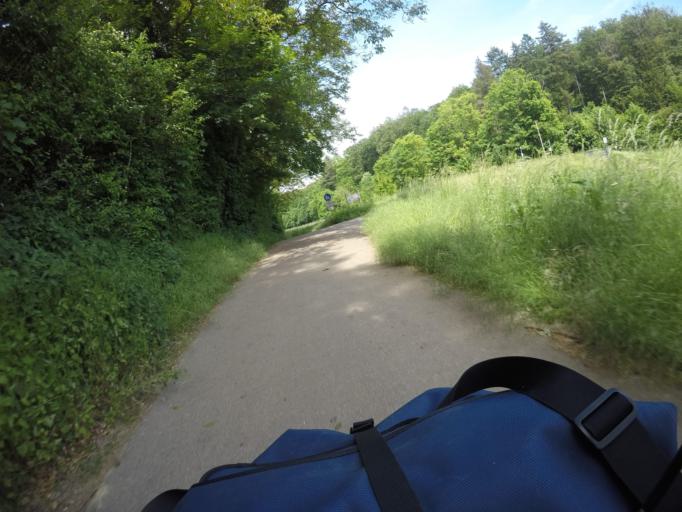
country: DE
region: Baden-Wuerttemberg
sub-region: Karlsruhe Region
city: Weingarten
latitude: 48.9789
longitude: 8.4961
